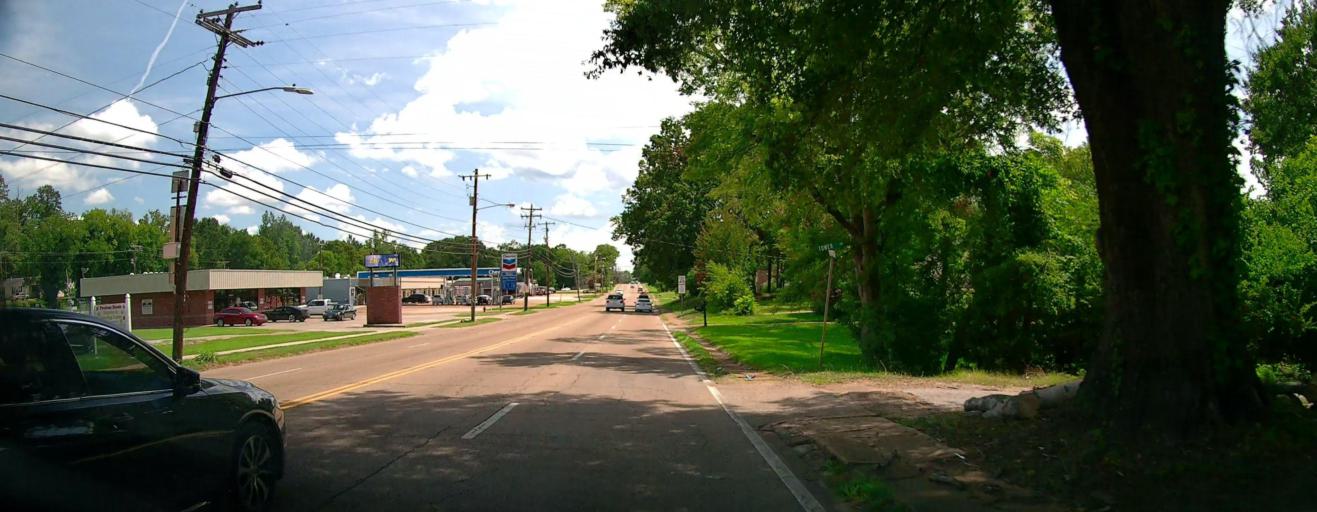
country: US
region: Mississippi
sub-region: Lee County
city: Verona
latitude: 34.2001
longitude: -88.7201
